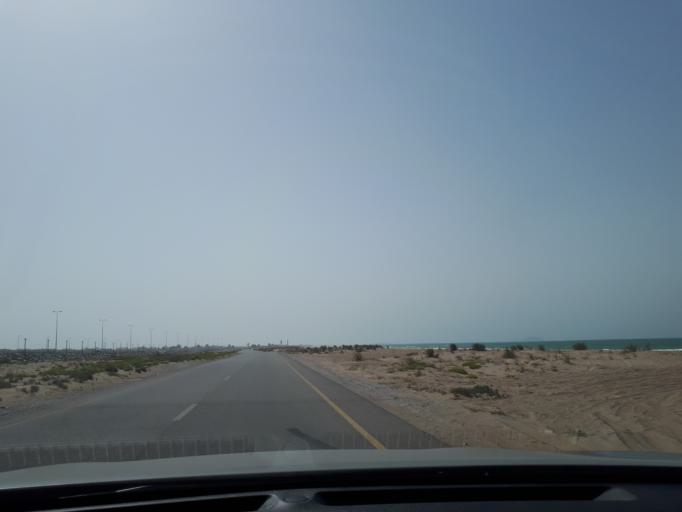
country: OM
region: Al Batinah
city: Barka'
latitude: 23.7150
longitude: 57.8689
